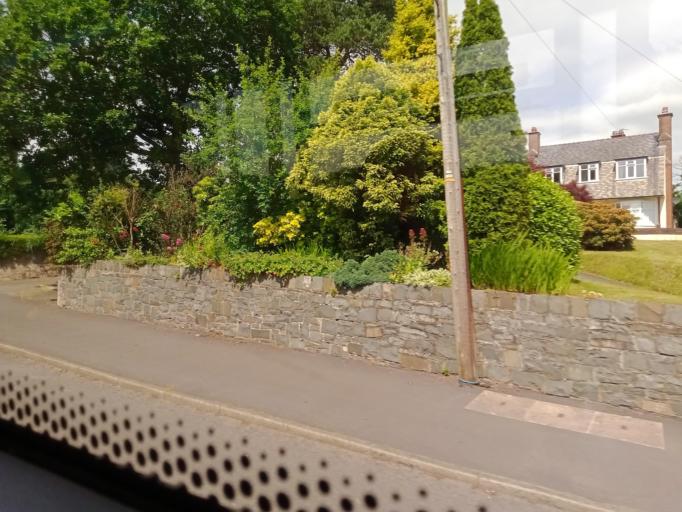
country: GB
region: Wales
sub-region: Gwynedd
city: Bangor
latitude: 53.2154
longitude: -4.1507
